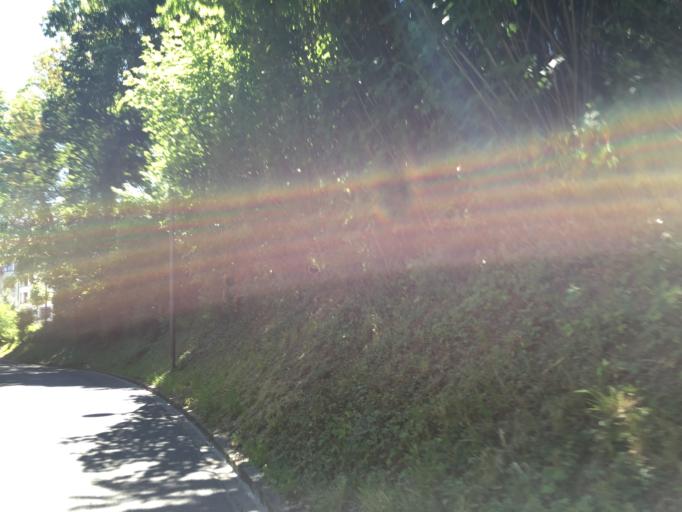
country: CH
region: Bern
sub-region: Bern-Mittelland District
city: Bern
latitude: 46.9575
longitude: 7.4383
